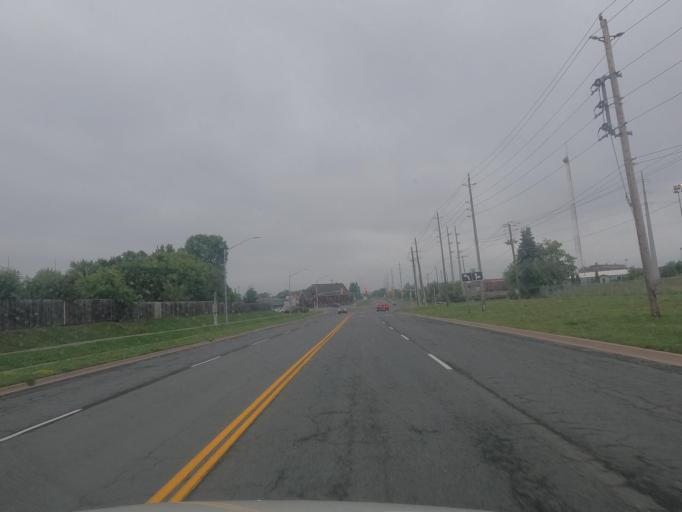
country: CA
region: Ontario
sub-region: Algoma
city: Sault Ste. Marie
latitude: 46.5281
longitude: -84.3479
